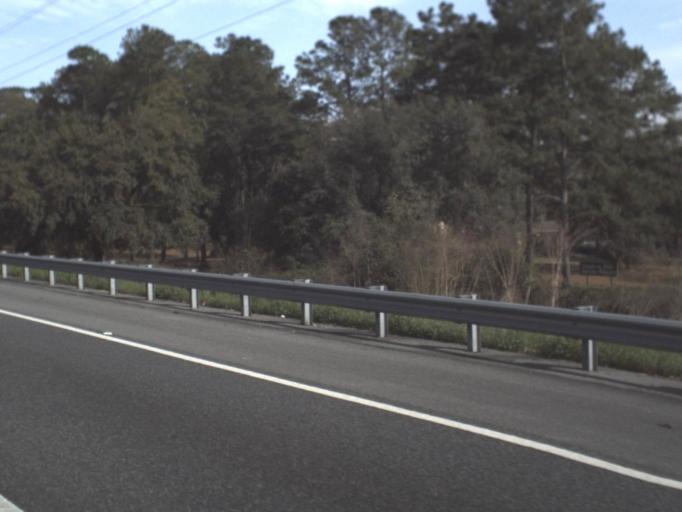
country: US
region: Florida
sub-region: Leon County
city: Tallahassee
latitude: 30.4806
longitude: -84.3169
